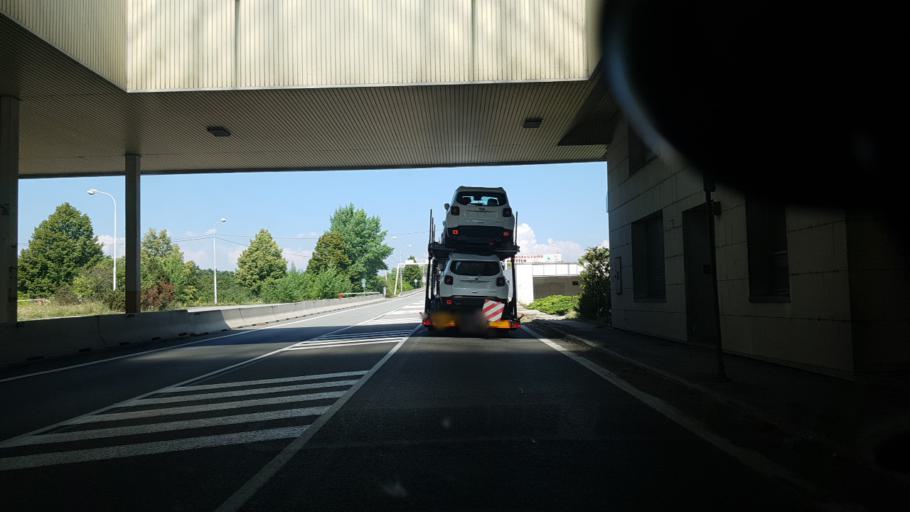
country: CZ
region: South Moravian
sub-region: Okres Breclav
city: Mikulov
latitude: 48.7896
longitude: 16.6362
